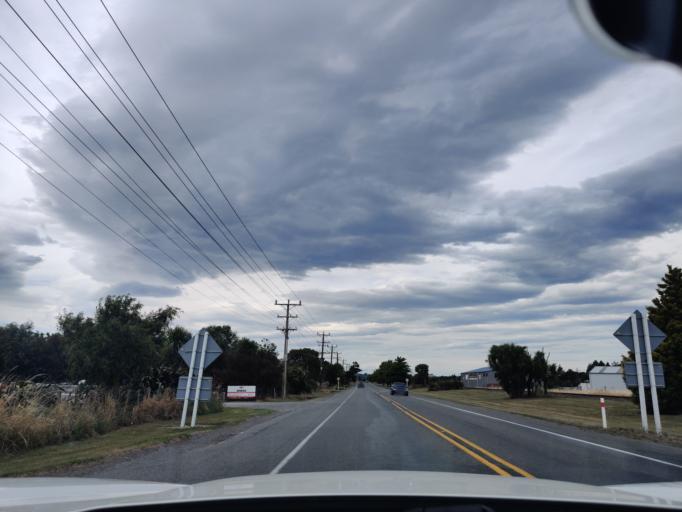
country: NZ
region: Wellington
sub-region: Masterton District
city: Masterton
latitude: -40.9569
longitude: 175.6161
